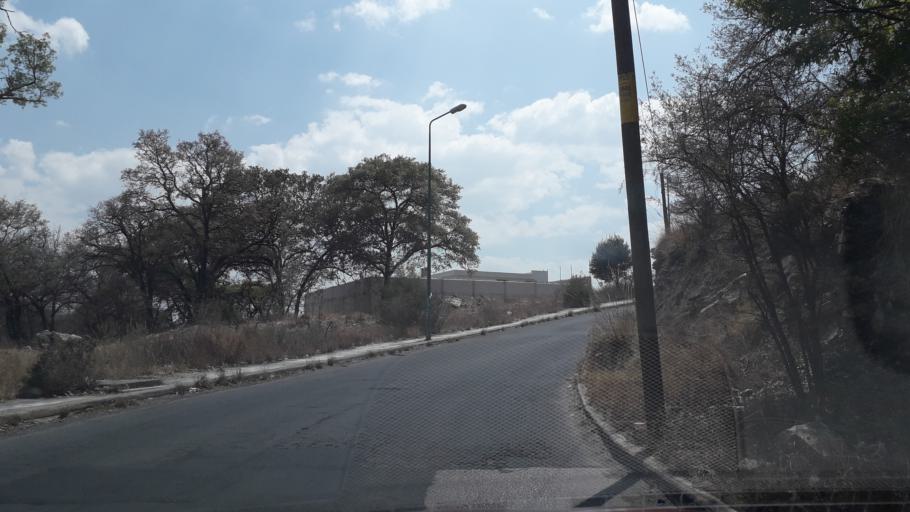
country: MX
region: Puebla
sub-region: Puebla
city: Galaxia la Calera
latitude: 18.9955
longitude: -98.1573
